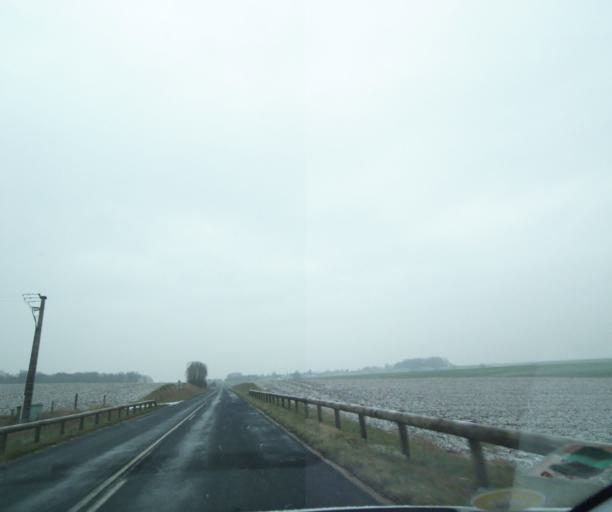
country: FR
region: Champagne-Ardenne
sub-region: Departement de la Haute-Marne
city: Wassy
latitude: 48.4698
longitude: 5.0242
